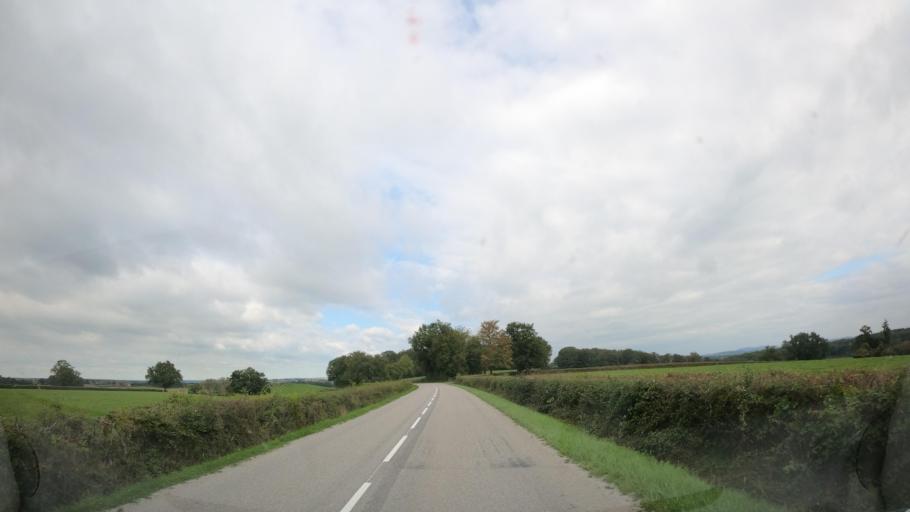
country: FR
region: Auvergne
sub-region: Departement de l'Allier
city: Saint-Gerand-le-Puy
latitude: 46.3075
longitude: 3.5778
